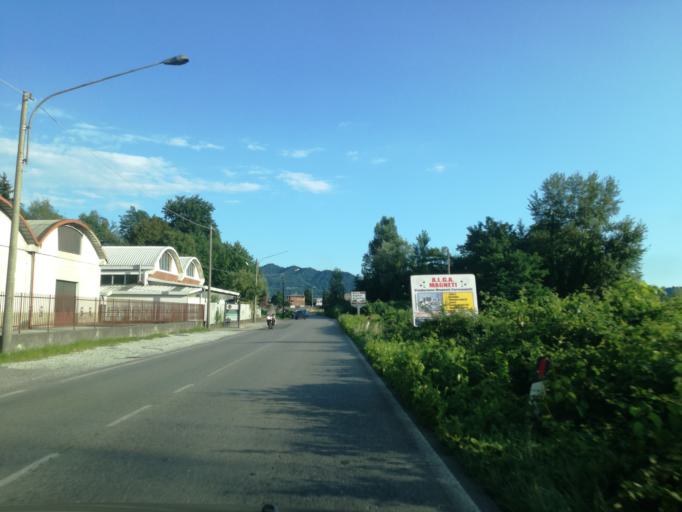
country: IT
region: Lombardy
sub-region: Provincia di Lecco
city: Monte Marenzo
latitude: 45.7667
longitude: 9.4454
